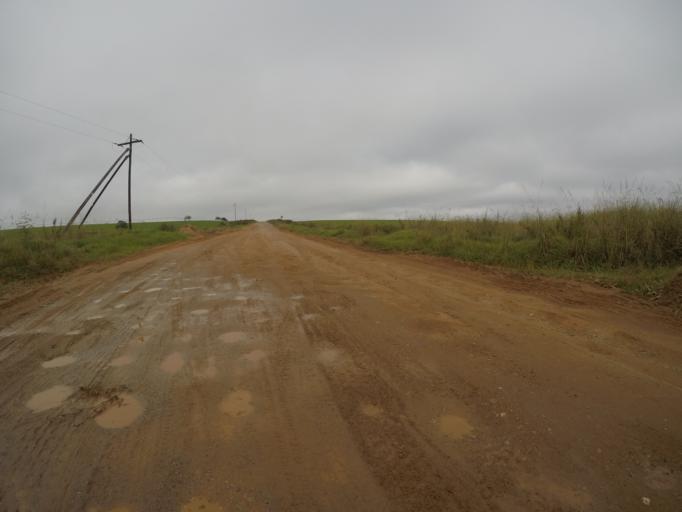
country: ZA
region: Eastern Cape
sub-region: Cacadu District Municipality
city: Kareedouw
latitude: -34.0190
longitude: 24.2393
